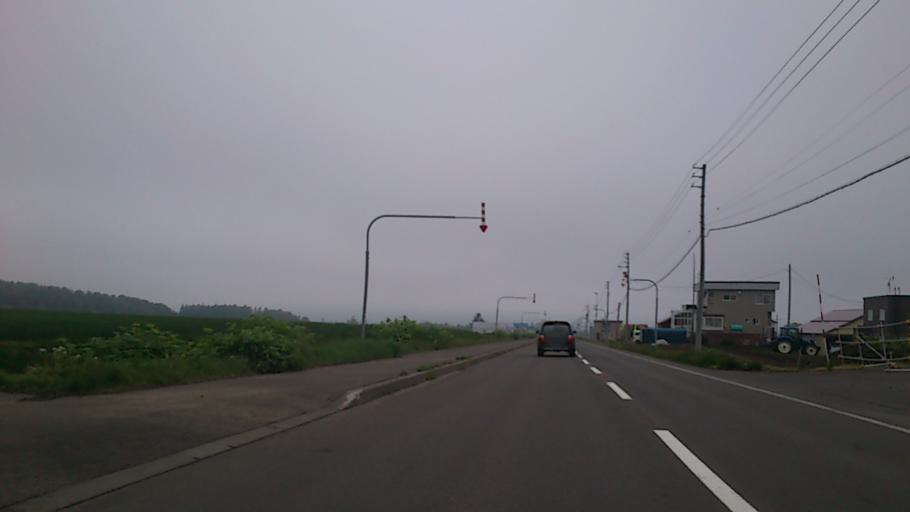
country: JP
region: Hokkaido
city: Niseko Town
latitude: 42.8820
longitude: 140.7900
